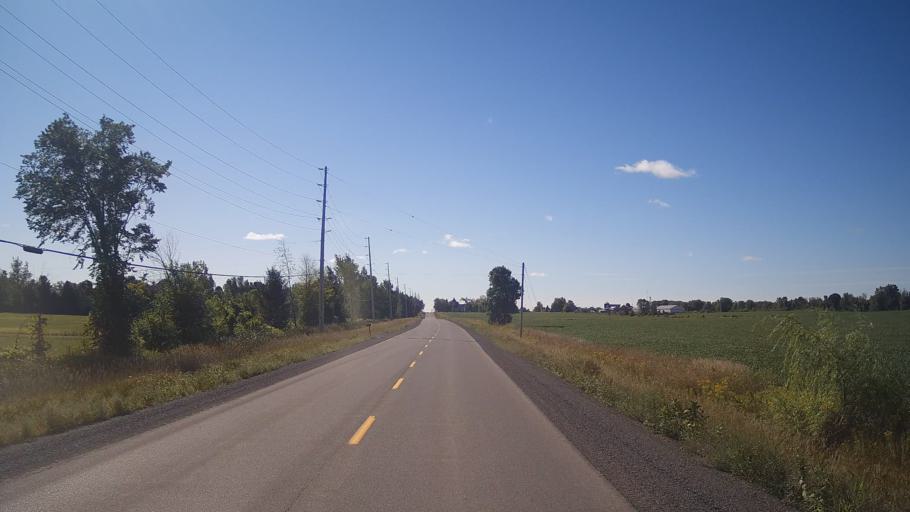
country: CA
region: Ontario
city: Prescott
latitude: 44.9767
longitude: -75.5377
